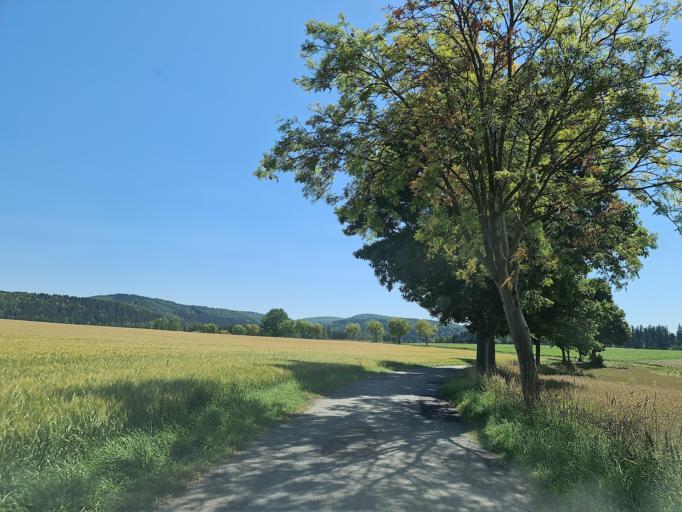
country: DE
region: Saxony
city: Neuhausen
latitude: 50.7007
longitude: 13.4977
